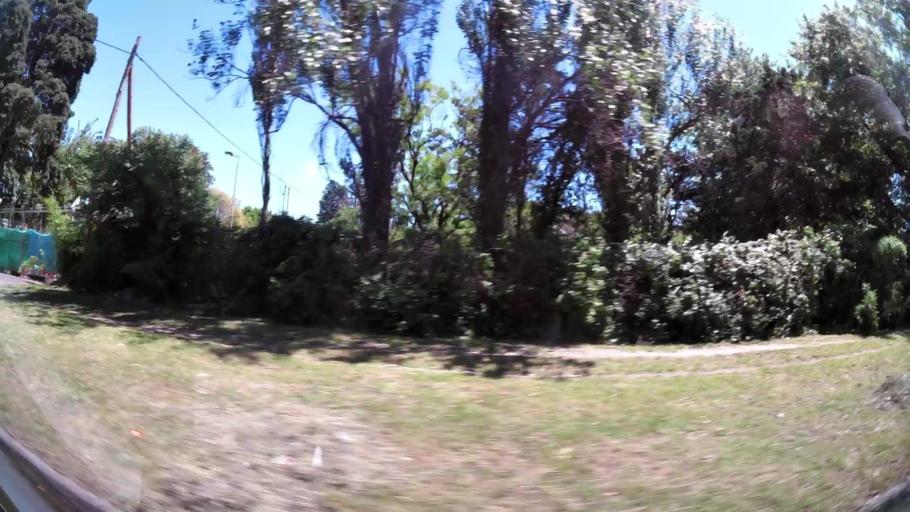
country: AR
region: Buenos Aires
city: Hurlingham
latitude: -34.5006
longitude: -58.6306
